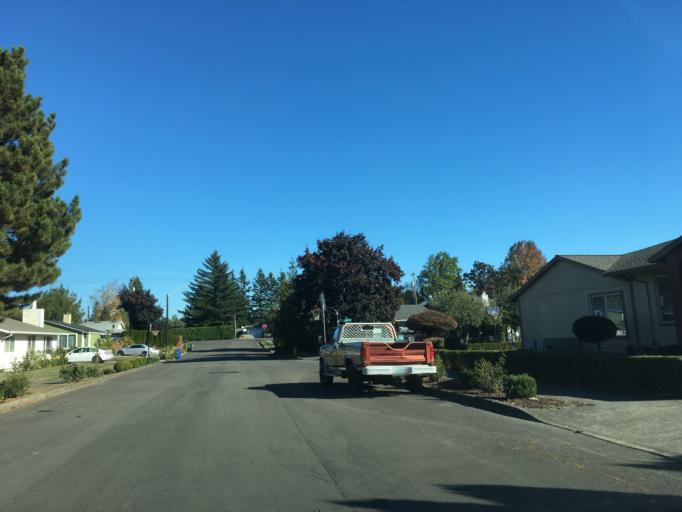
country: US
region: Oregon
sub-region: Multnomah County
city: Gresham
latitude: 45.4941
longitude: -122.4004
